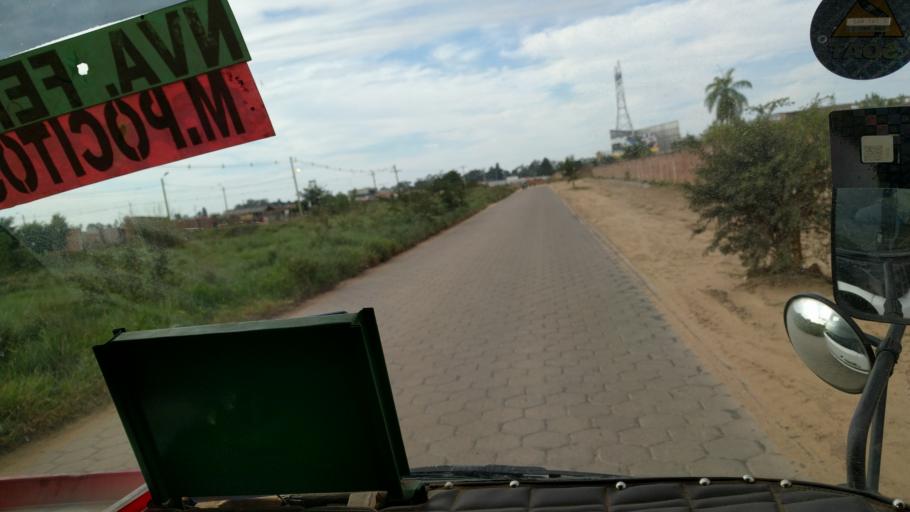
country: BO
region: Santa Cruz
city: Santa Cruz de la Sierra
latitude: -17.6922
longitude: -63.1438
